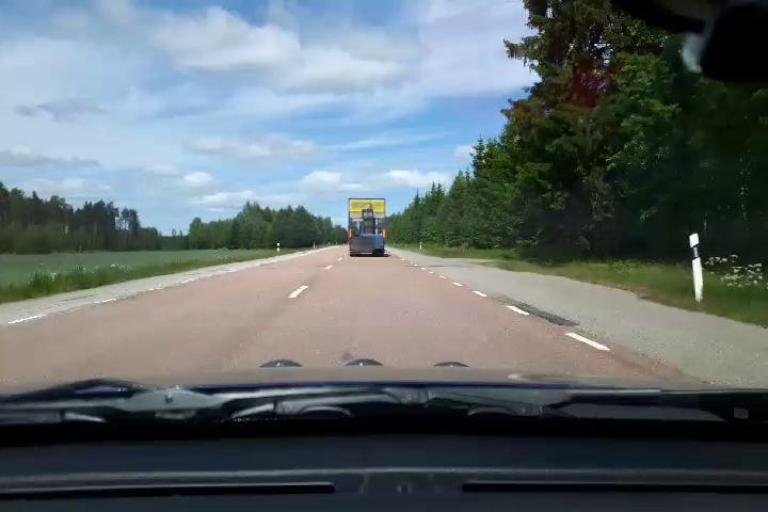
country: SE
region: Uppsala
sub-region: Osthammars Kommun
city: Bjorklinge
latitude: 60.1573
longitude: 17.4911
